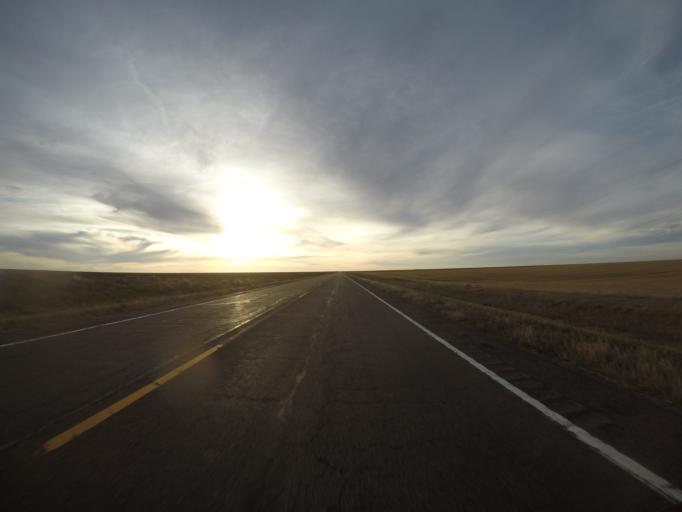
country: US
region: Colorado
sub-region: Washington County
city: Akron
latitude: 39.7274
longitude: -103.1352
